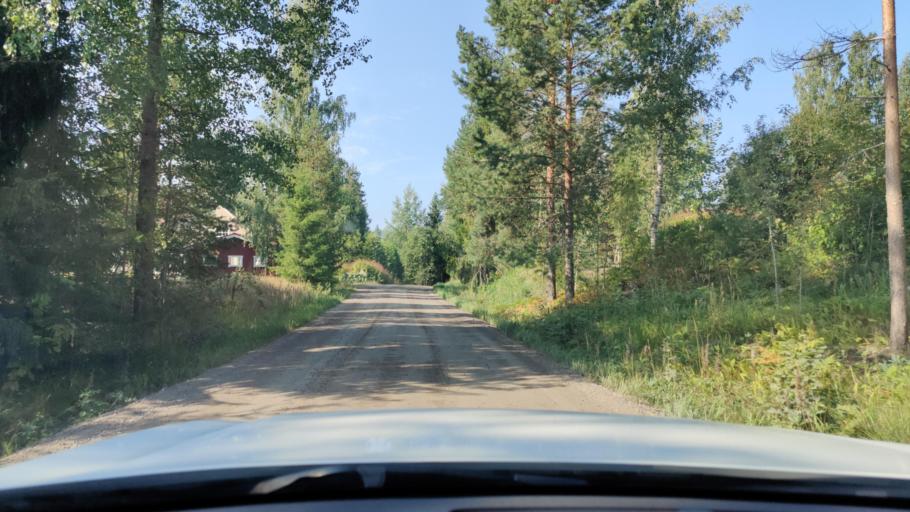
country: FI
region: Haeme
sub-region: Riihimaeki
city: Loppi
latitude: 60.6762
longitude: 24.5733
